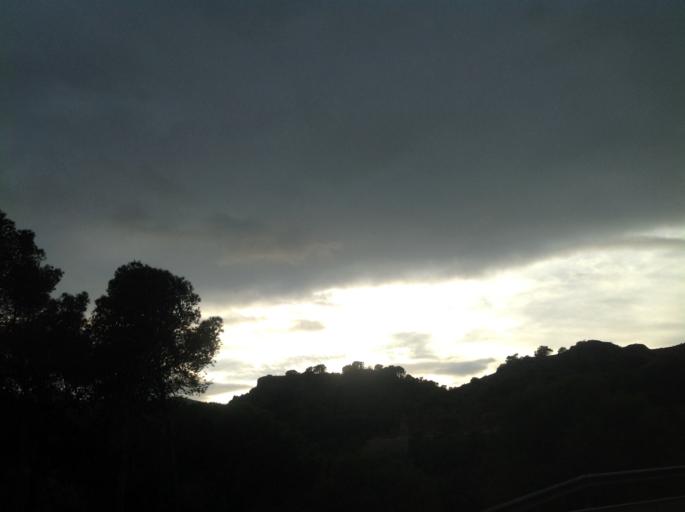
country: ES
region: Andalusia
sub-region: Provincia de Malaga
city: Ardales
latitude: 36.9132
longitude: -4.7896
